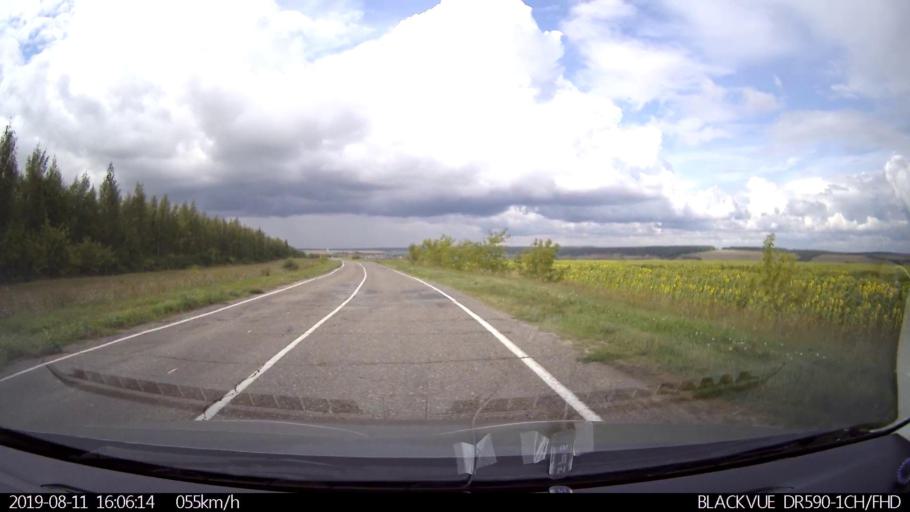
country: RU
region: Ulyanovsk
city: Ignatovka
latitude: 53.9672
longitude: 47.6491
